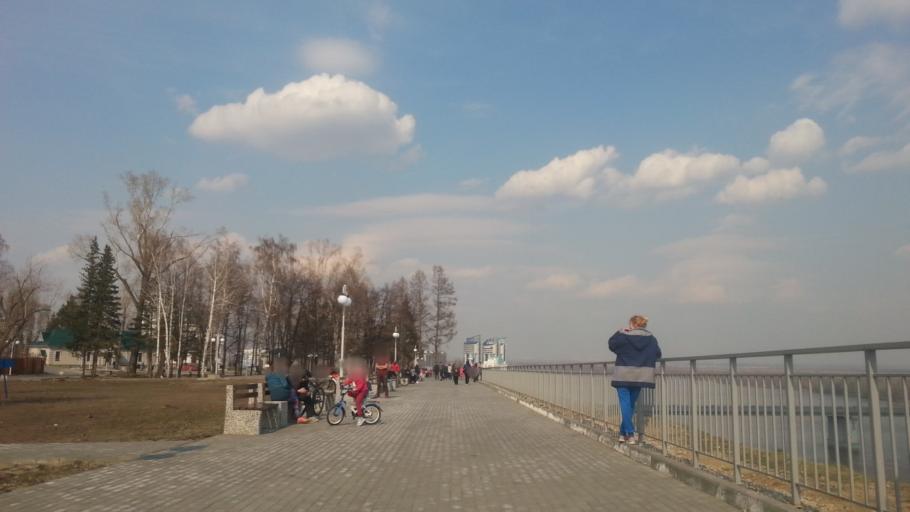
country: RU
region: Altai Krai
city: Zaton
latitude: 53.3214
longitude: 83.7947
